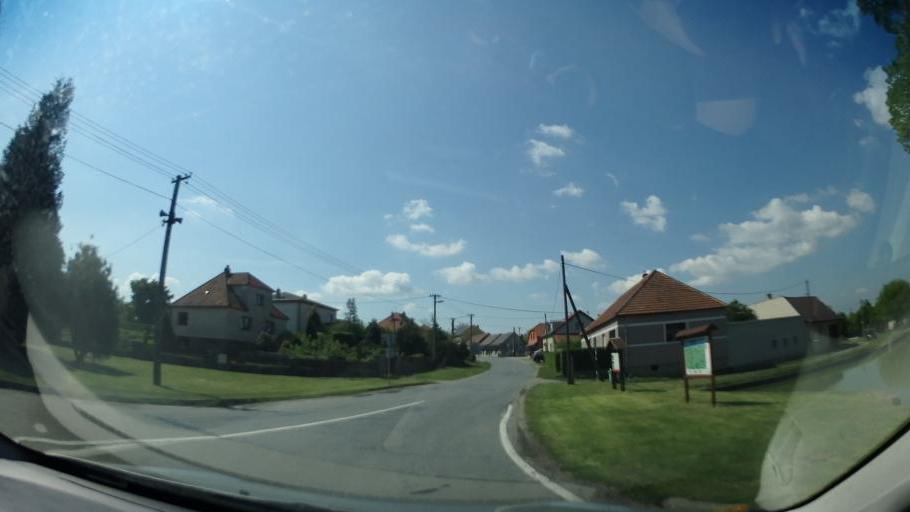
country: CZ
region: Vysocina
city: Hrotovice
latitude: 49.1806
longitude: 16.0832
